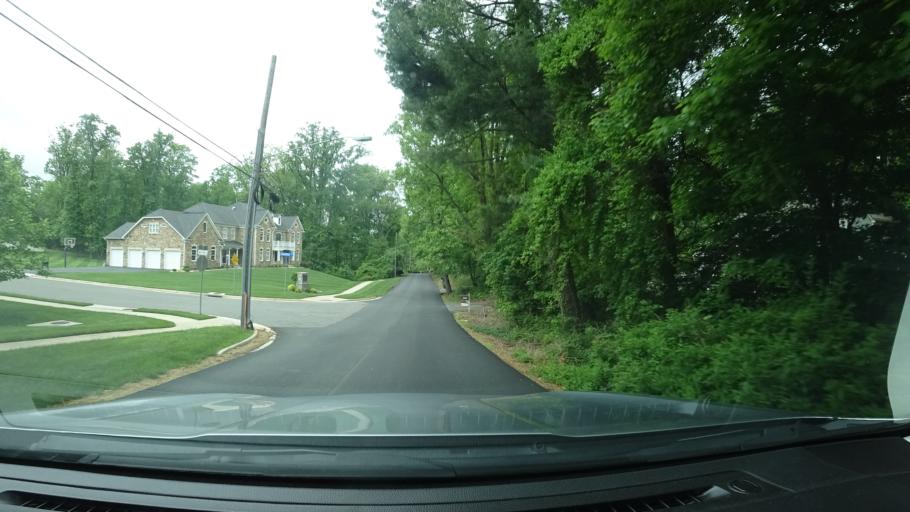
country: US
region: Virginia
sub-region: City of Fairfax
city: Fairfax
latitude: 38.8666
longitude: -77.3400
